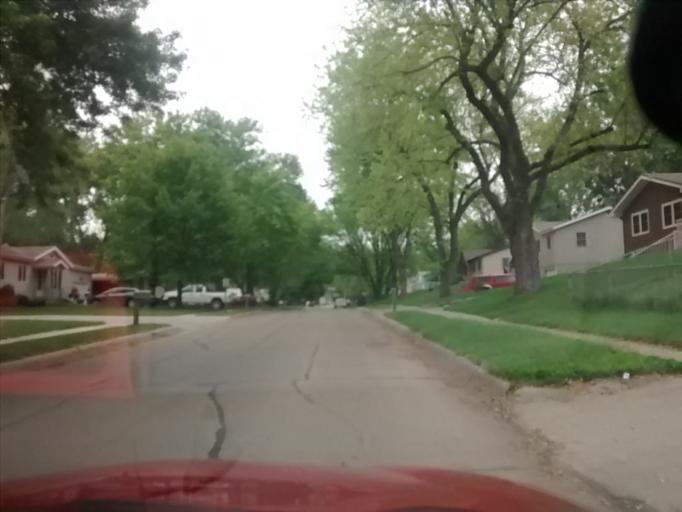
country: US
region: Nebraska
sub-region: Sarpy County
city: Bellevue
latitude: 41.1708
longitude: -95.9236
